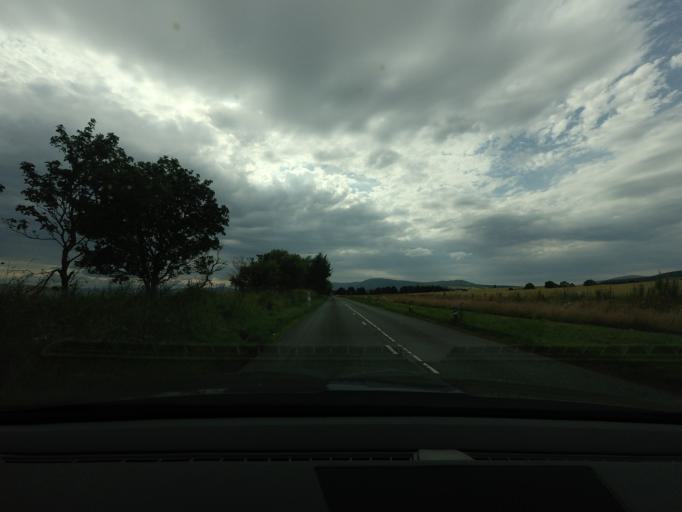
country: GB
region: Scotland
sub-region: Highland
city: Alness
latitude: 57.6915
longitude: -4.2135
